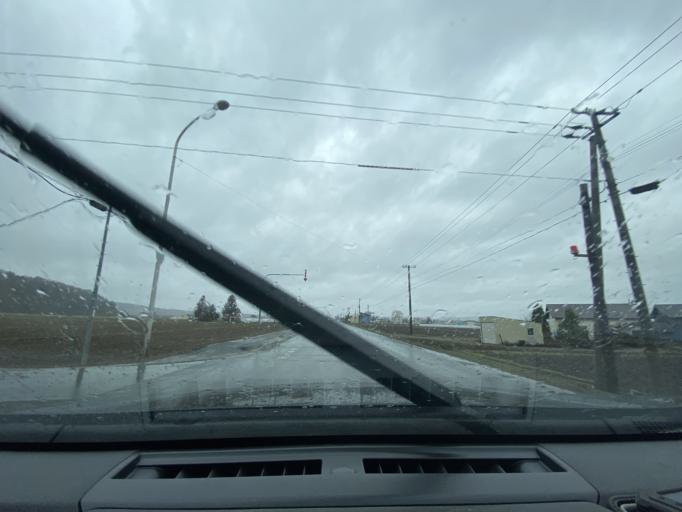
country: JP
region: Hokkaido
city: Fukagawa
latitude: 43.8083
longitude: 142.0339
